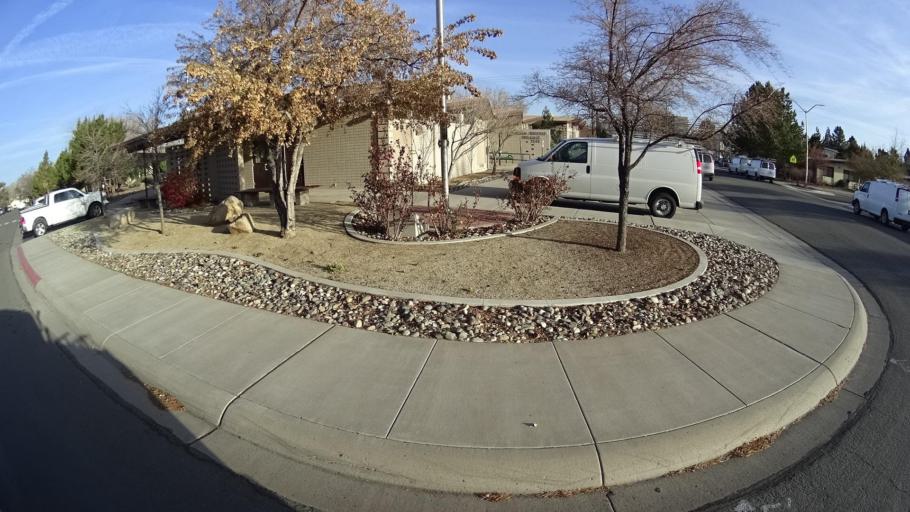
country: US
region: Nevada
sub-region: Washoe County
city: Sparks
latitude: 39.5414
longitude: -119.7816
